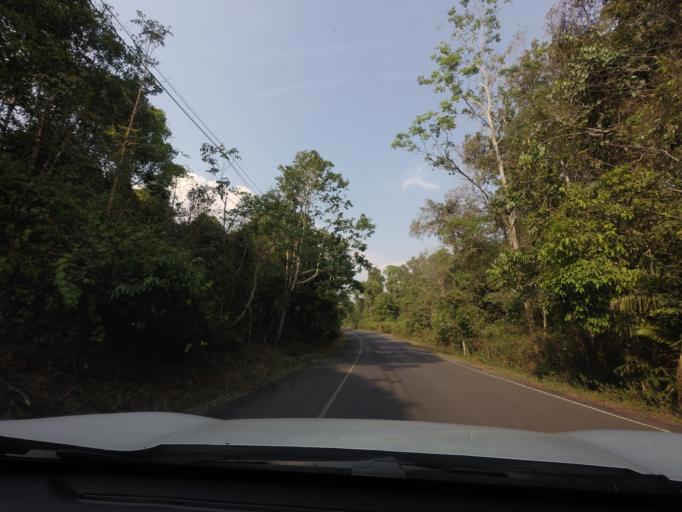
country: TH
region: Nakhon Nayok
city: Nakhon Nayok
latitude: 14.4135
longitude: 101.3780
